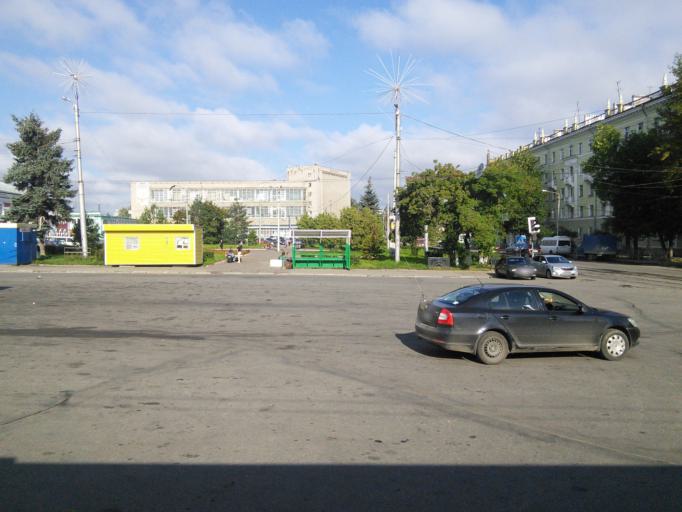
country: RU
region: Vologda
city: Vologda
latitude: 59.2072
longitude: 39.8845
